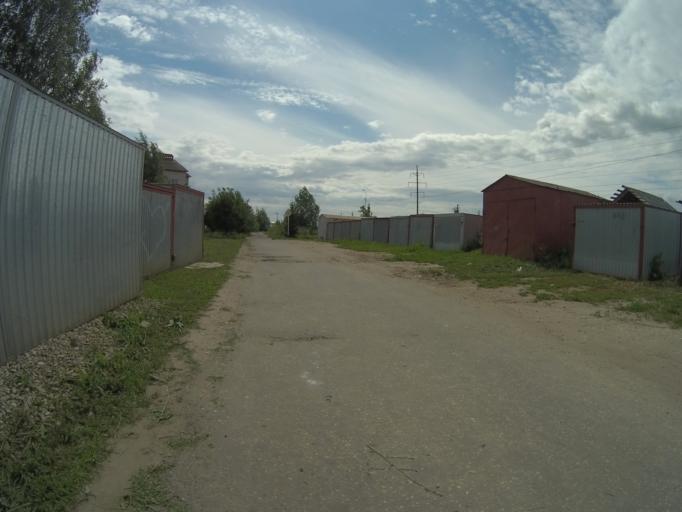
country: RU
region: Vladimir
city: Bogolyubovo
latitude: 56.1997
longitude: 40.5272
